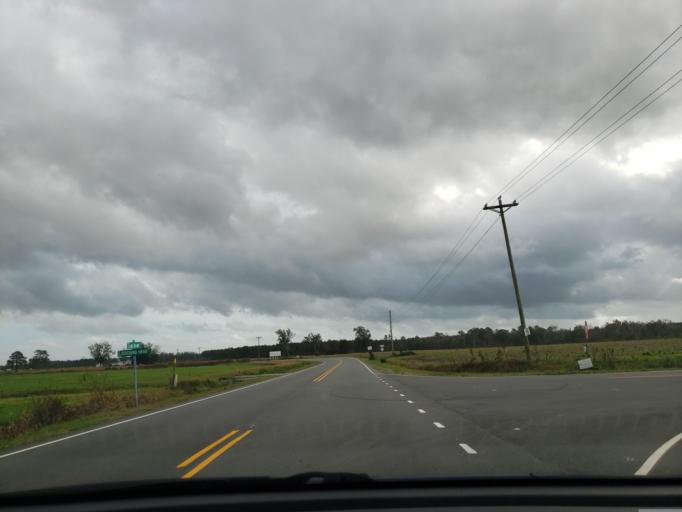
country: US
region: North Carolina
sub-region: Duplin County
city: Kenansville
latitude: 34.8913
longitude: -77.9073
